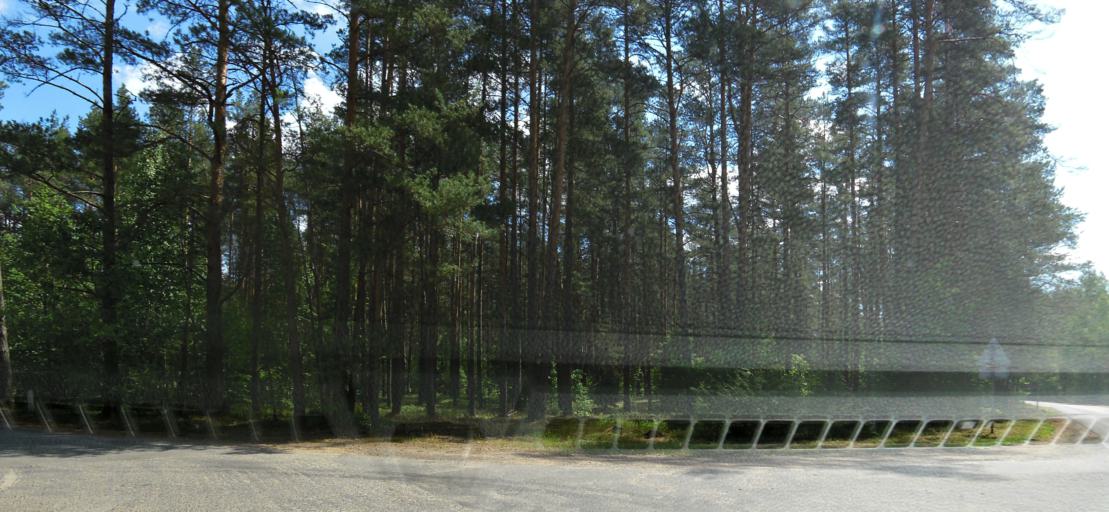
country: LT
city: Nemencine
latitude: 54.8208
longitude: 25.4002
